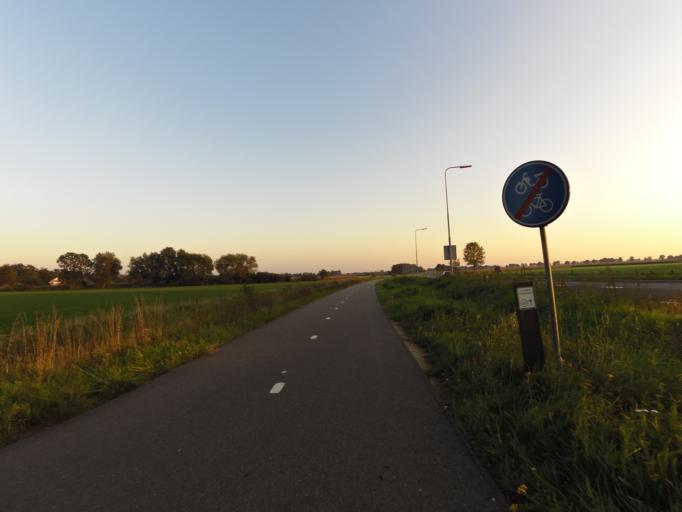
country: NL
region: Gelderland
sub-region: Gemeente Doetinchem
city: Doetinchem
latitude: 51.9417
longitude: 6.3129
